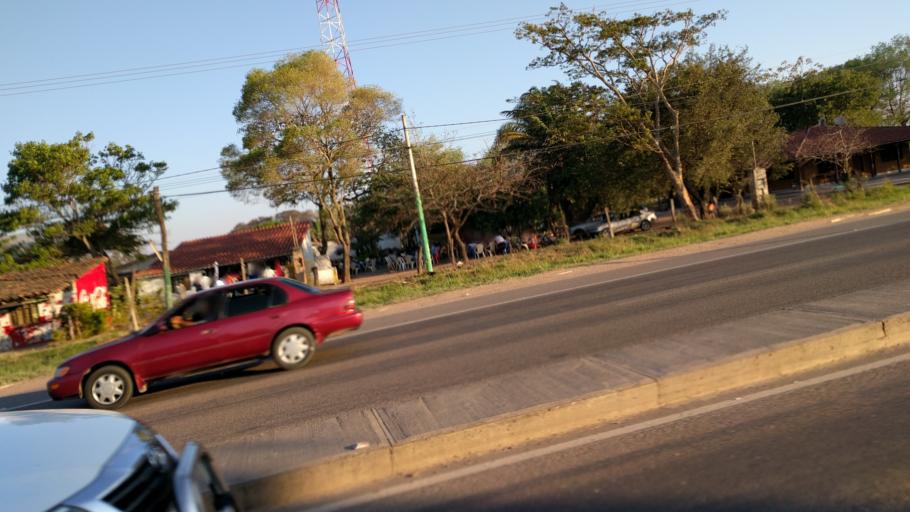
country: BO
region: Santa Cruz
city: Cotoca
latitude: -17.7614
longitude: -63.0226
